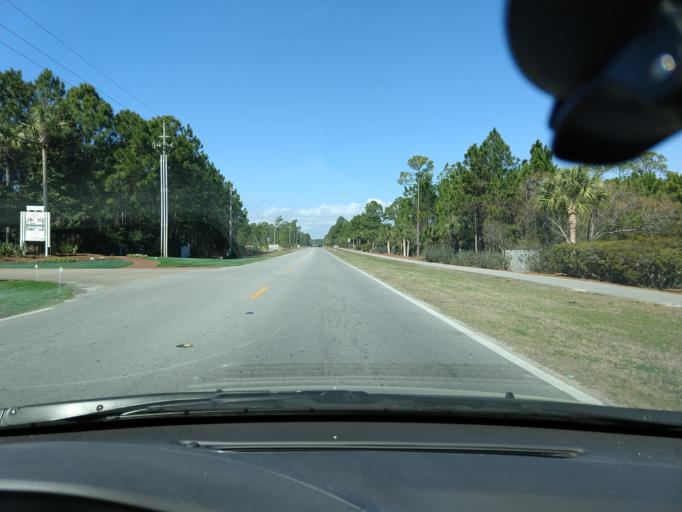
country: US
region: Florida
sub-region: Walton County
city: Miramar Beach
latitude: 30.3647
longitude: -86.2665
